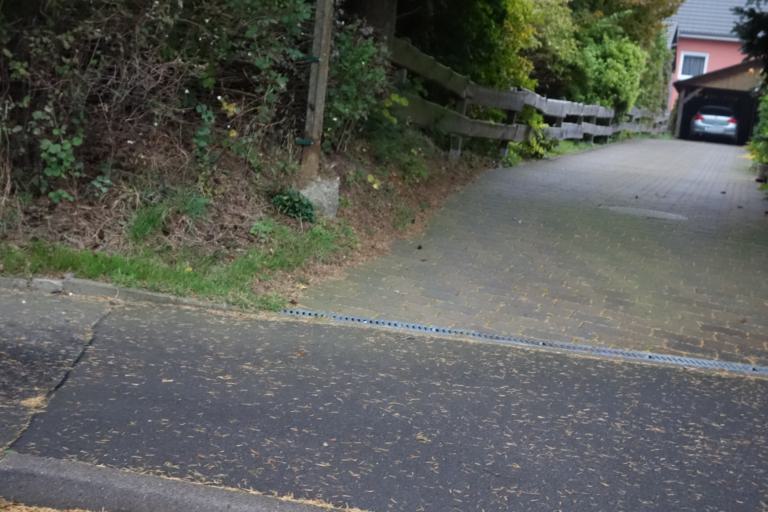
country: DE
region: Saxony
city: Freiberg
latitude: 50.9193
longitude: 13.3535
